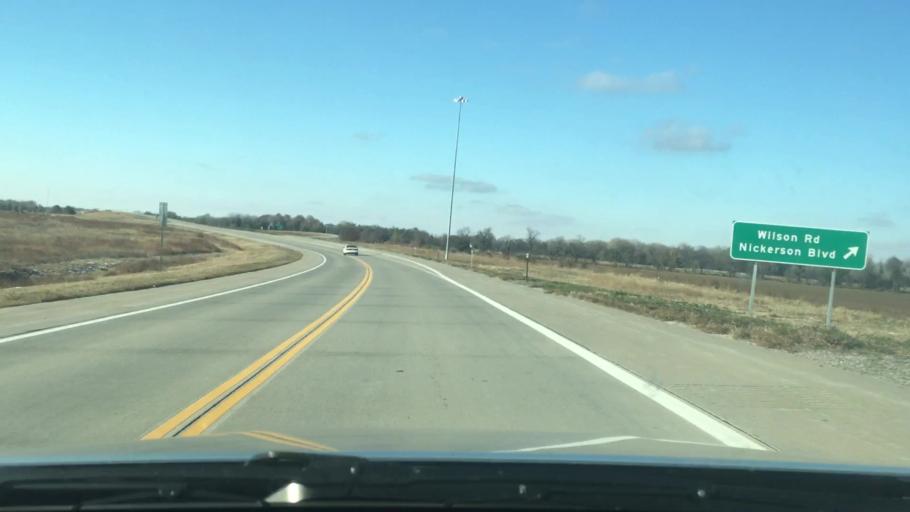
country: US
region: Kansas
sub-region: Reno County
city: Hutchinson
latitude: 38.0863
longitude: -97.9909
